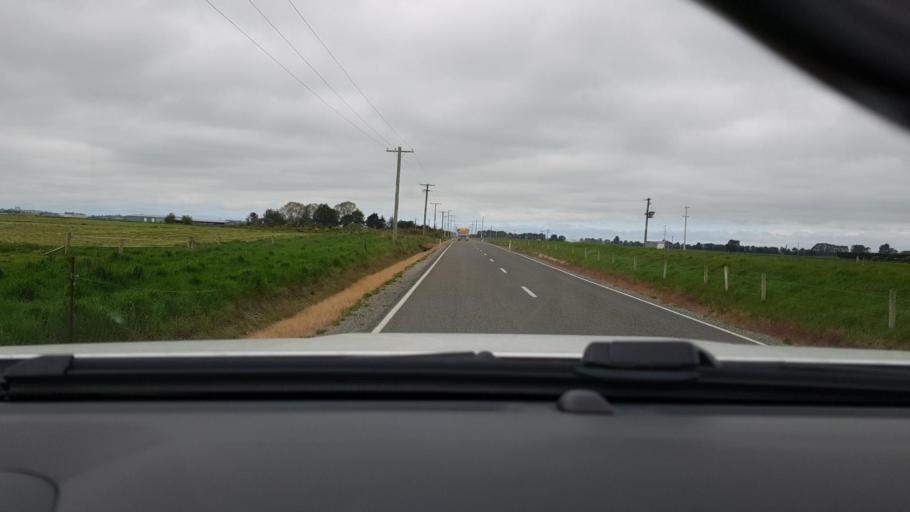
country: NZ
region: Otago
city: Oamaru
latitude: -44.9648
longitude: 170.9726
